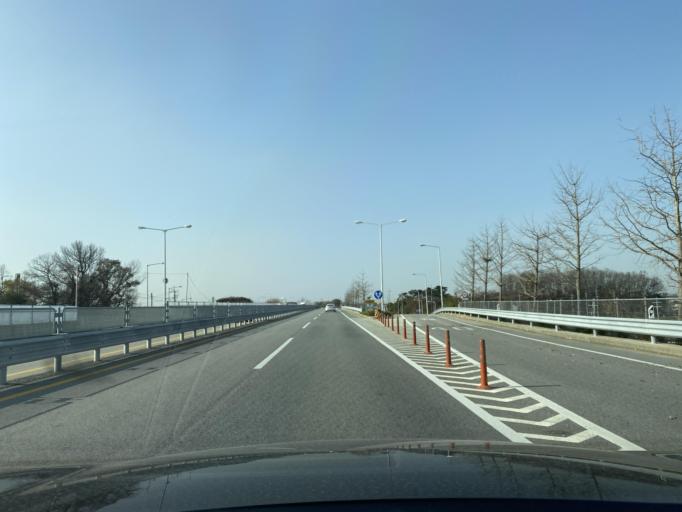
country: KR
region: Chungcheongnam-do
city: Yesan
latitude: 36.7578
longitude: 126.8230
